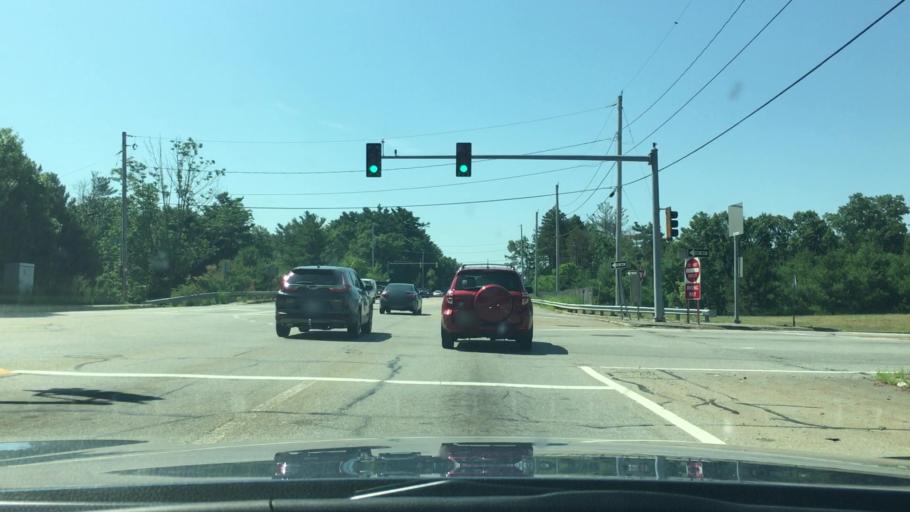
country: US
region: Massachusetts
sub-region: Middlesex County
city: Billerica
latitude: 42.5635
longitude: -71.2973
